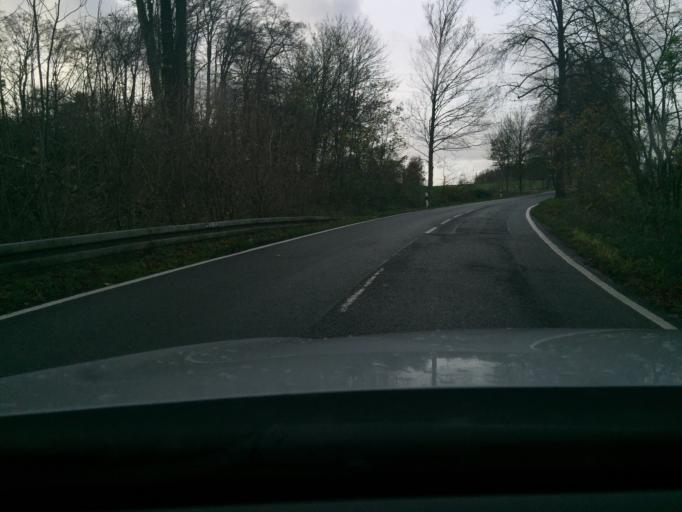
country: DE
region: North Rhine-Westphalia
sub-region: Regierungsbezirk Dusseldorf
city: Velbert
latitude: 51.3691
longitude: 7.0647
